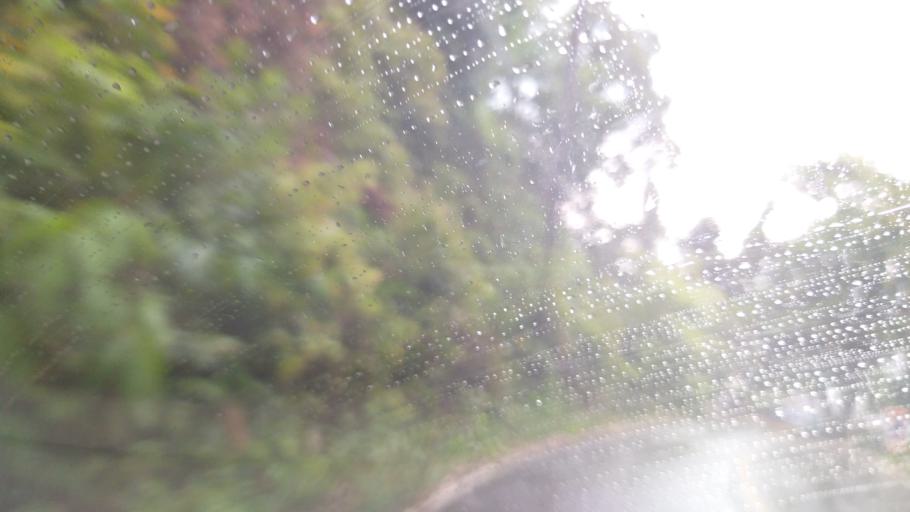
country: TH
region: Trat
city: Ko Chang Tai
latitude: 11.9752
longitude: 102.3197
